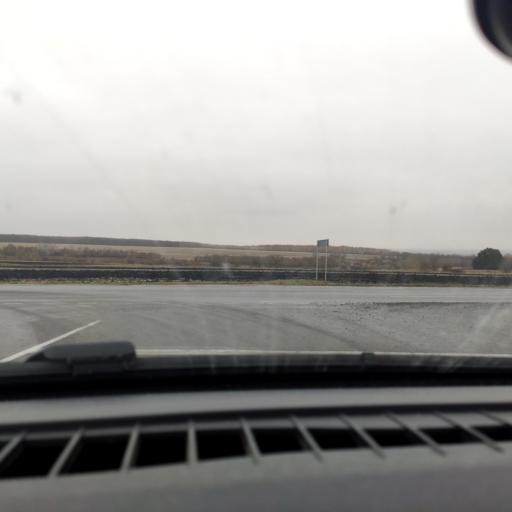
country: RU
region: Voronezj
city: Ostrogozhsk
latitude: 50.9004
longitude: 39.0679
